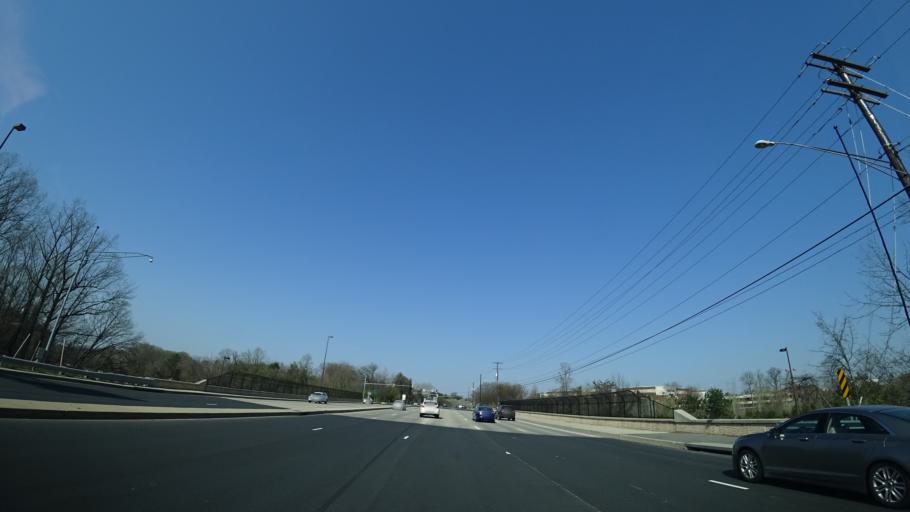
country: US
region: Maryland
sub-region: Montgomery County
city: North Bethesda
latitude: 39.0217
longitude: -77.1420
